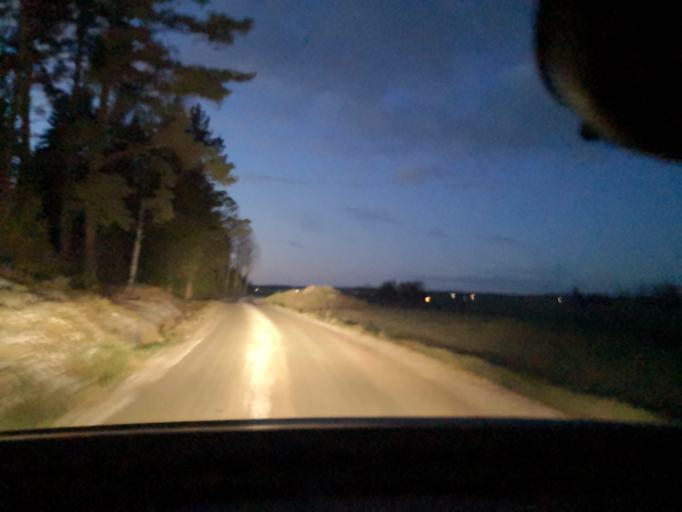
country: SE
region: Uppsala
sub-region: Heby Kommun
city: Heby
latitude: 59.9146
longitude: 16.7510
